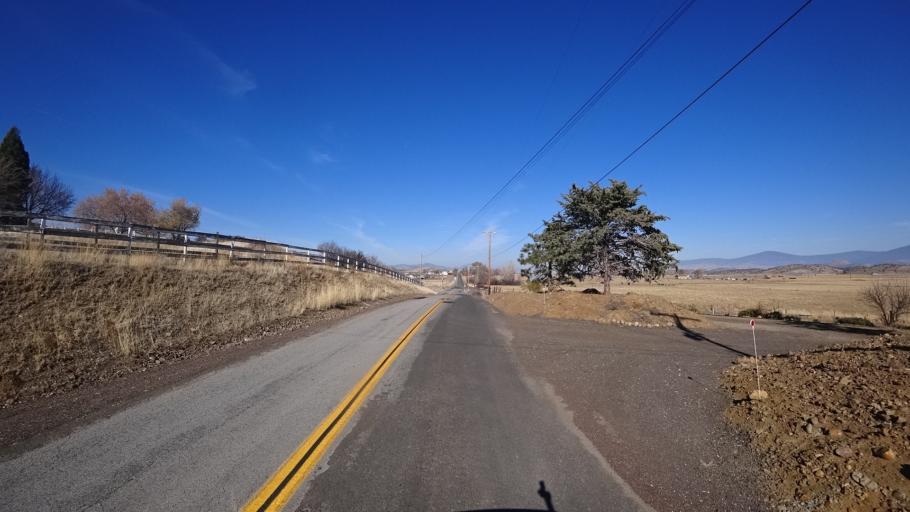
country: US
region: California
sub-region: Siskiyou County
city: Montague
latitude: 41.6077
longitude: -122.5302
